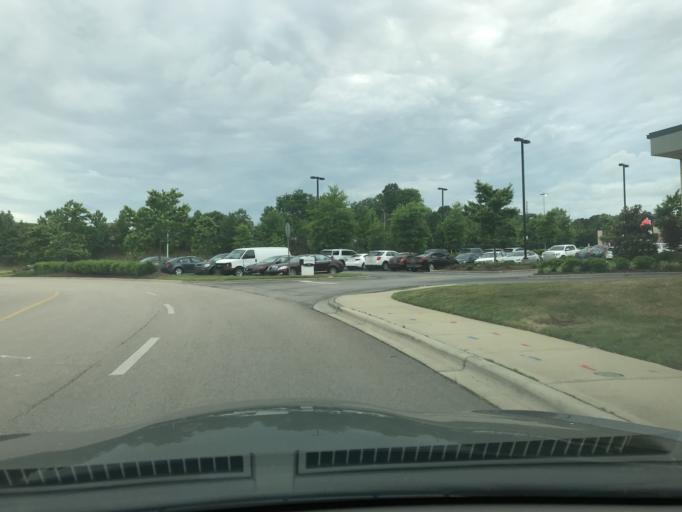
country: US
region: North Carolina
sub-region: Wake County
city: Raleigh
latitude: 35.8670
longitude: -78.5797
